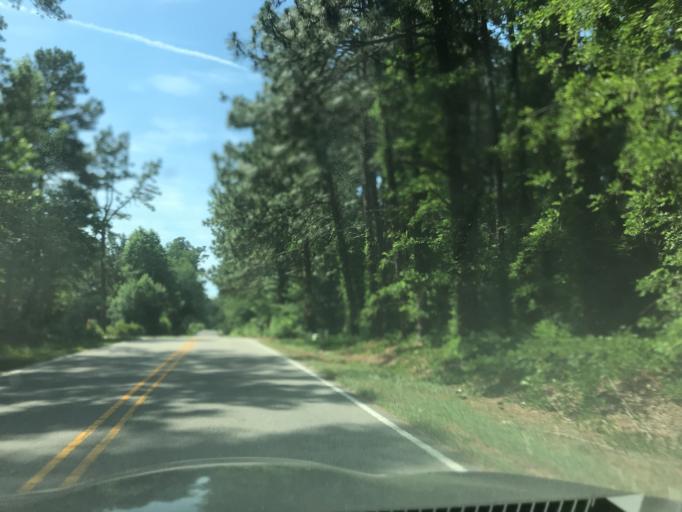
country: US
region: North Carolina
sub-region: Wake County
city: Wendell
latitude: 35.7682
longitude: -78.3550
